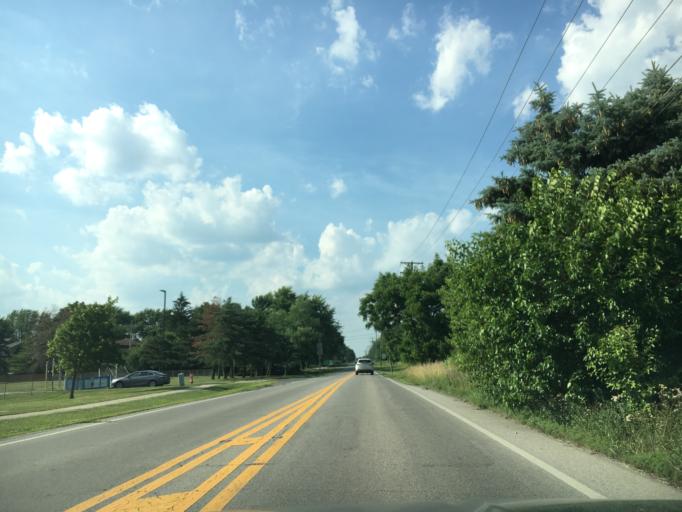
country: US
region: Ohio
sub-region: Franklin County
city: Lincoln Village
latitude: 39.9840
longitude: -83.1651
